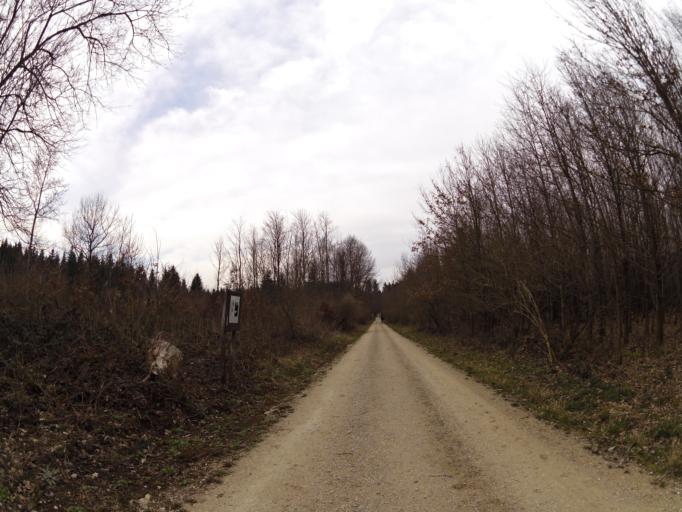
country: CH
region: Aargau
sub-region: Bezirk Aarau
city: Oberentfelden
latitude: 47.3723
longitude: 8.0341
